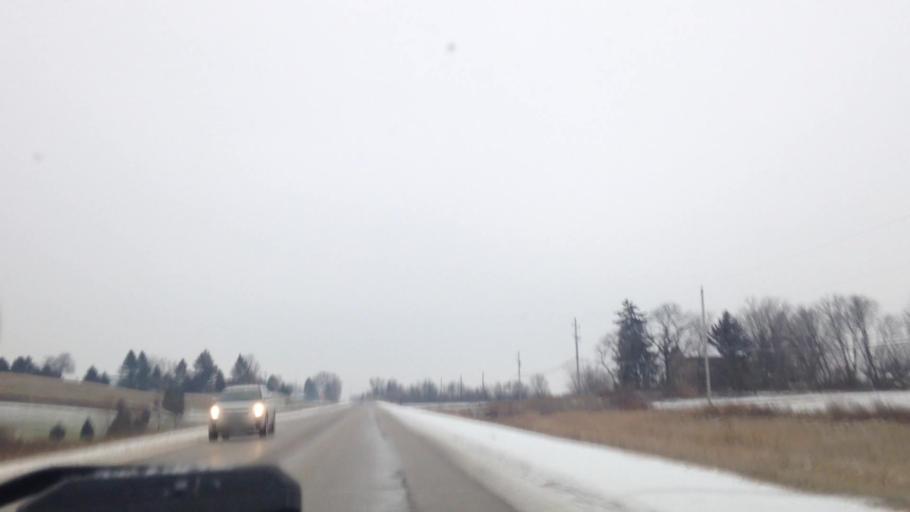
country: US
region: Wisconsin
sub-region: Dodge County
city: Mayville
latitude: 43.4331
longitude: -88.5421
